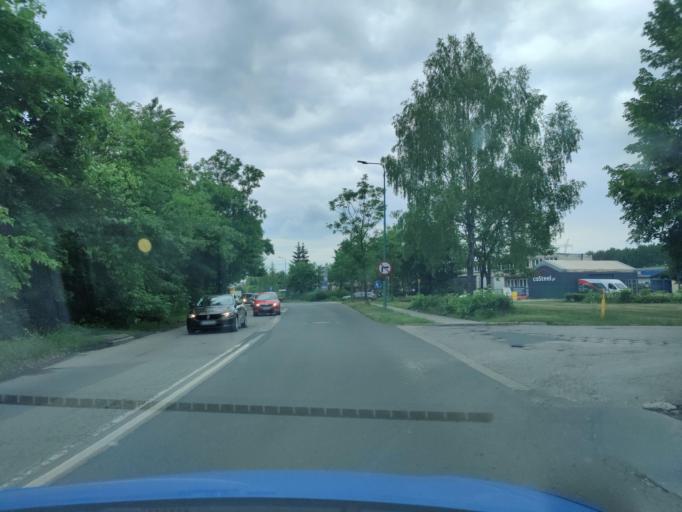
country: PL
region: Silesian Voivodeship
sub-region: Myslowice
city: Myslowice
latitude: 50.2466
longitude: 19.1533
